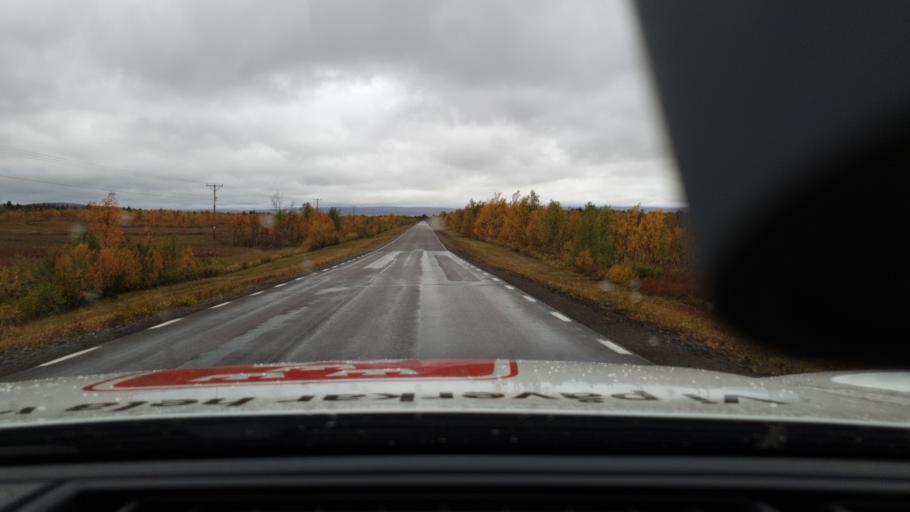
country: SE
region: Norrbotten
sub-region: Kiruna Kommun
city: Kiruna
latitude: 67.7686
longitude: 20.1630
